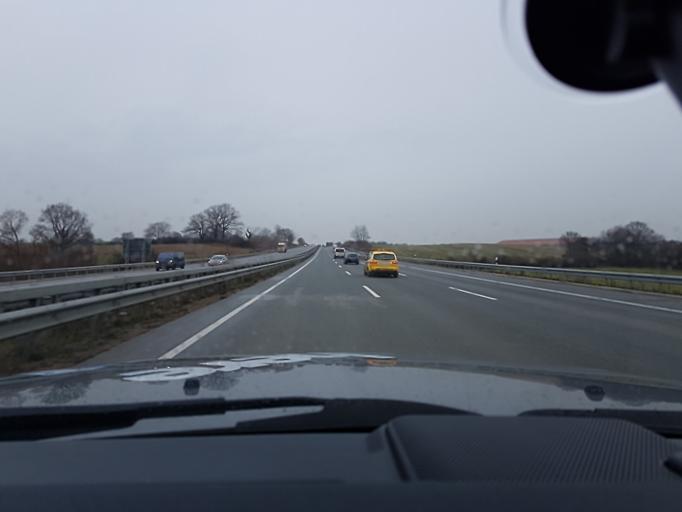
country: DE
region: Schleswig-Holstein
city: Meddewade
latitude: 53.7931
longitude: 10.4315
